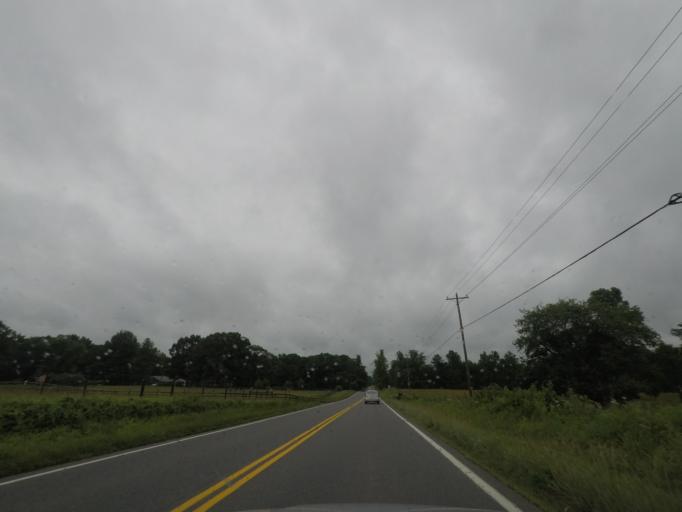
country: US
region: Virginia
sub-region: Fluvanna County
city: Palmyra
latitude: 37.9313
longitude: -78.2486
